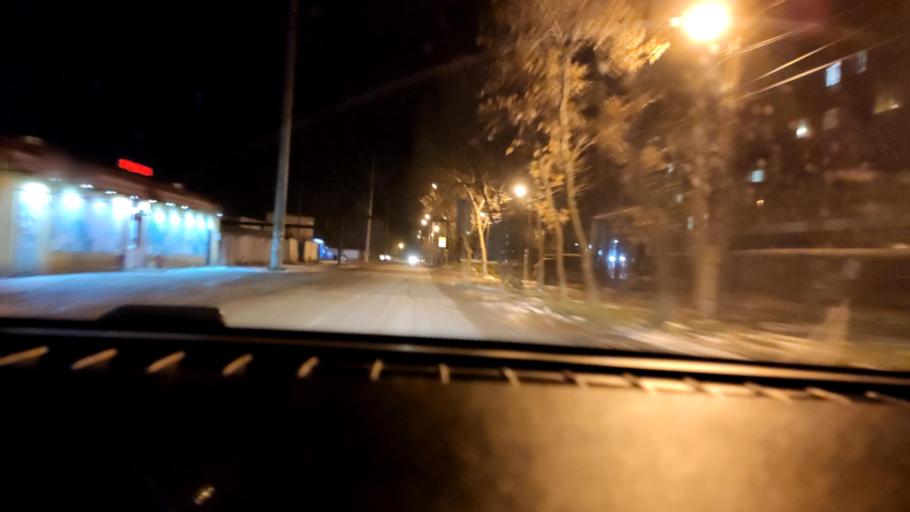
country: RU
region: Samara
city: Samara
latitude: 53.1373
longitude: 50.1538
